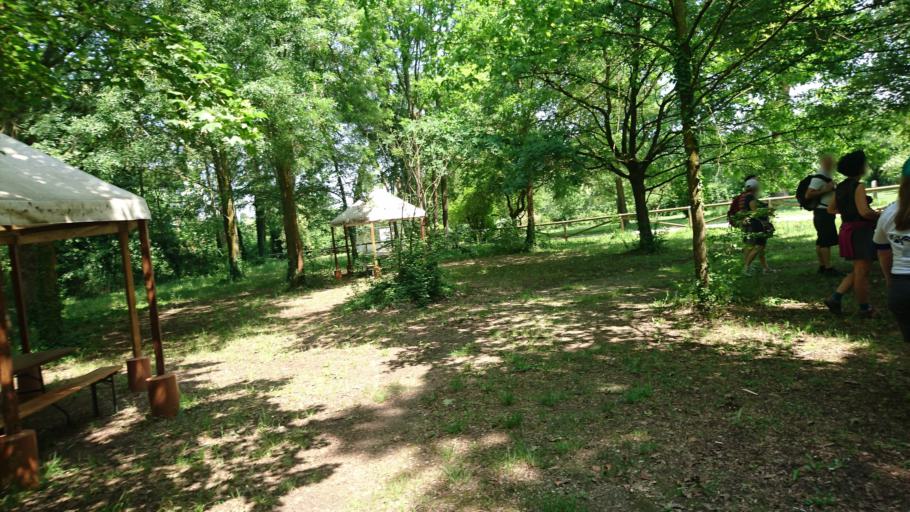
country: IT
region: Veneto
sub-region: Provincia di Venezia
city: Campagna Lupia
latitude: 45.3645
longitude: 12.1387
